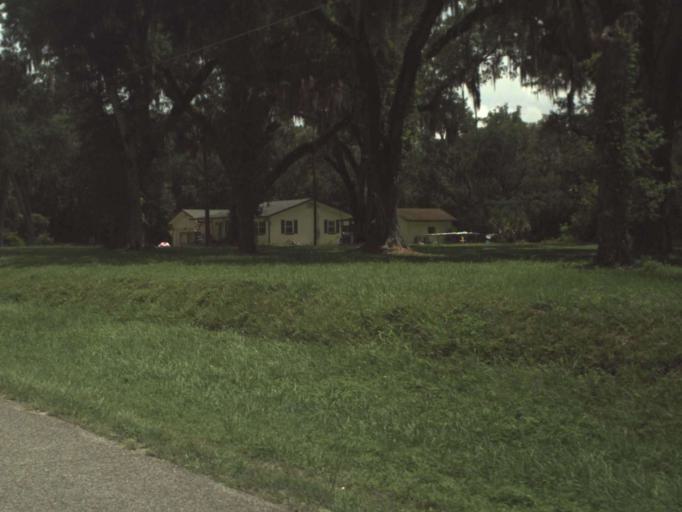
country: US
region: Florida
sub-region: Sumter County
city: Wildwood
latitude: 28.8201
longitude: -82.0455
